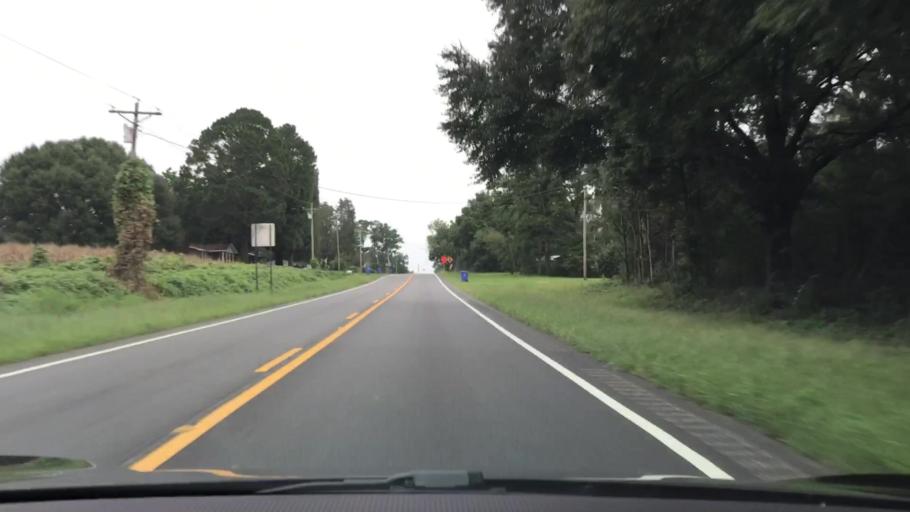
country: US
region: Alabama
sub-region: Covington County
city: Opp
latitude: 31.2770
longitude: -86.1580
